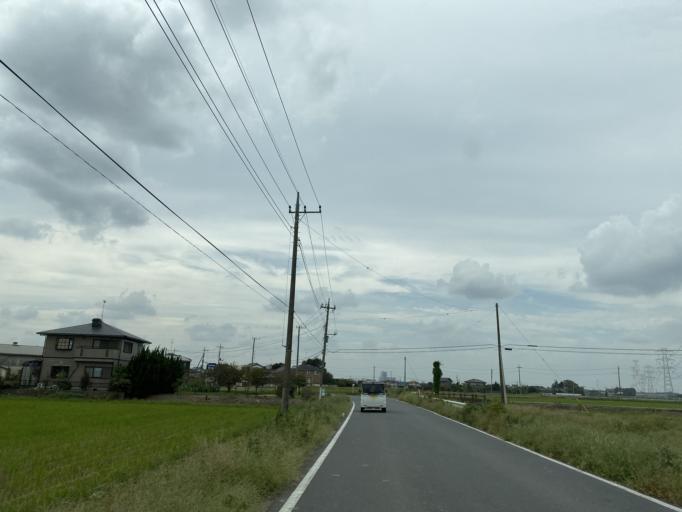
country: JP
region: Ibaraki
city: Moriya
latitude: 35.9731
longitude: 140.0329
